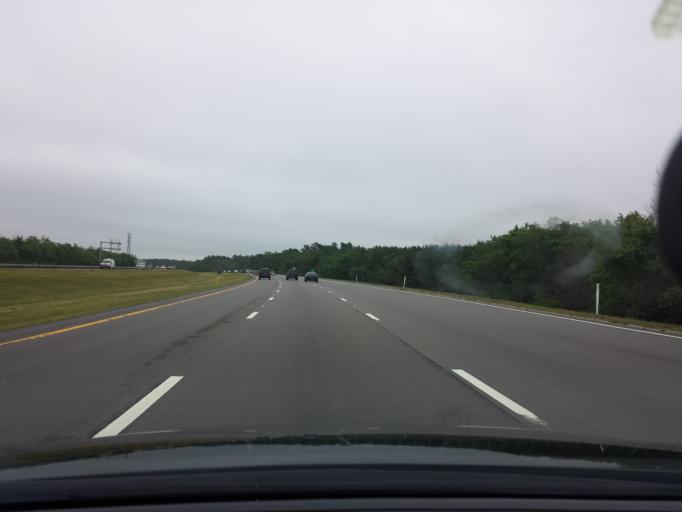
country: US
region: Massachusetts
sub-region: Plymouth County
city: Onset
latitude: 41.7639
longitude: -70.6661
